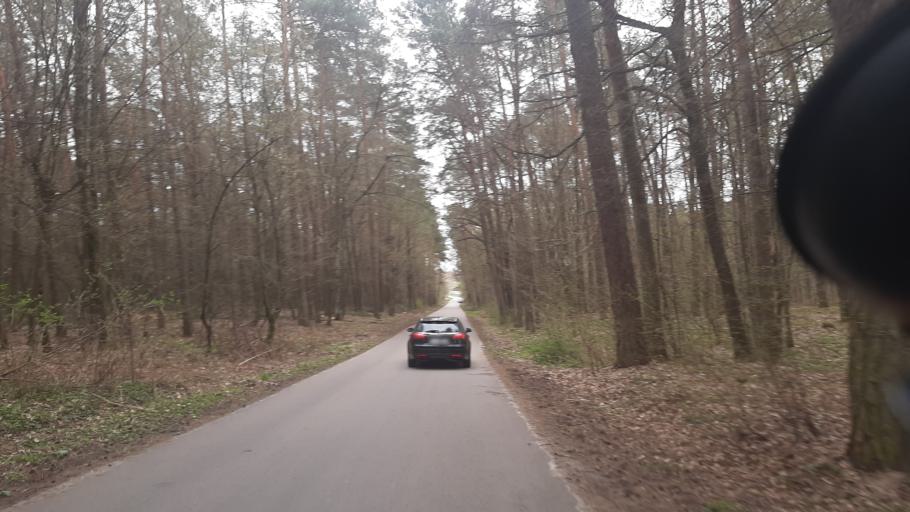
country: PL
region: Lublin Voivodeship
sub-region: Powiat lubelski
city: Niemce
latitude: 51.3715
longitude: 22.5524
